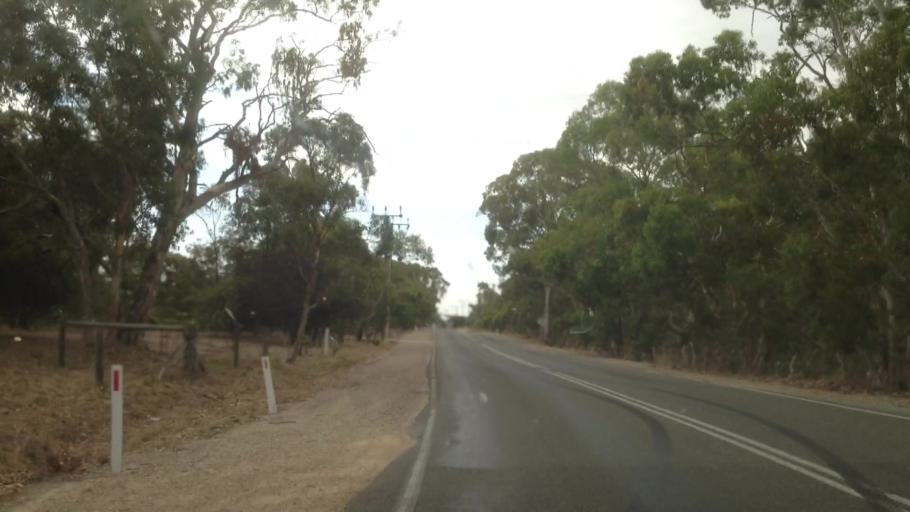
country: AU
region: South Australia
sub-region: Barossa
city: Williamstown
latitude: -34.6432
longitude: 138.8584
